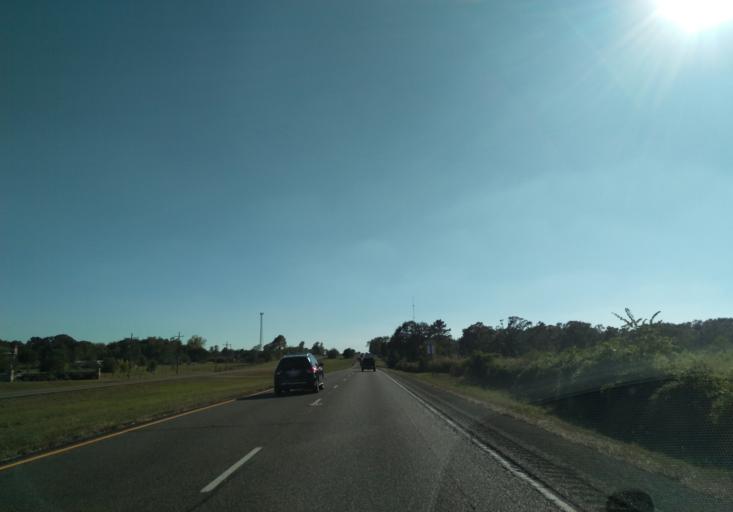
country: US
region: Texas
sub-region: Grimes County
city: Navasota
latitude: 30.2620
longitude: -96.0428
